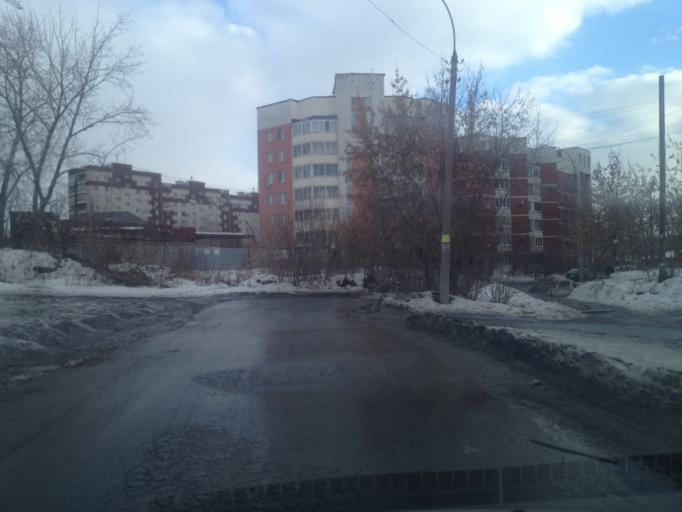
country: RU
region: Sverdlovsk
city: Yekaterinburg
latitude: 56.8549
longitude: 60.5820
